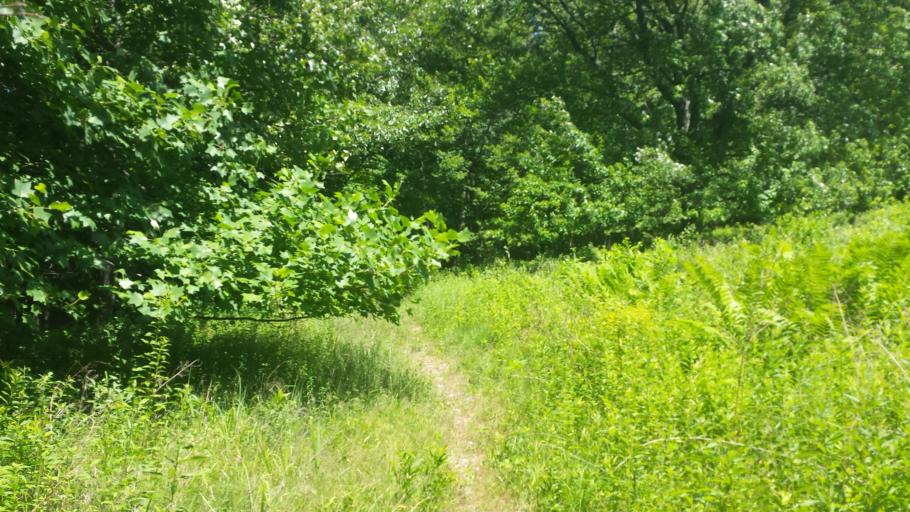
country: US
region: New York
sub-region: Westchester County
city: Pound Ridge
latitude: 41.2551
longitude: -73.5822
